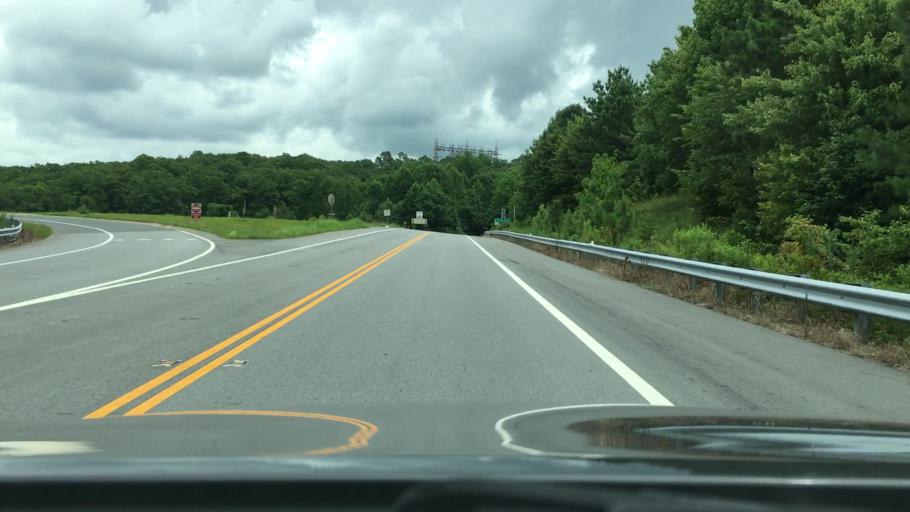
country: US
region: Virginia
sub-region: Amherst County
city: Madison Heights
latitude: 37.4070
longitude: -79.0819
